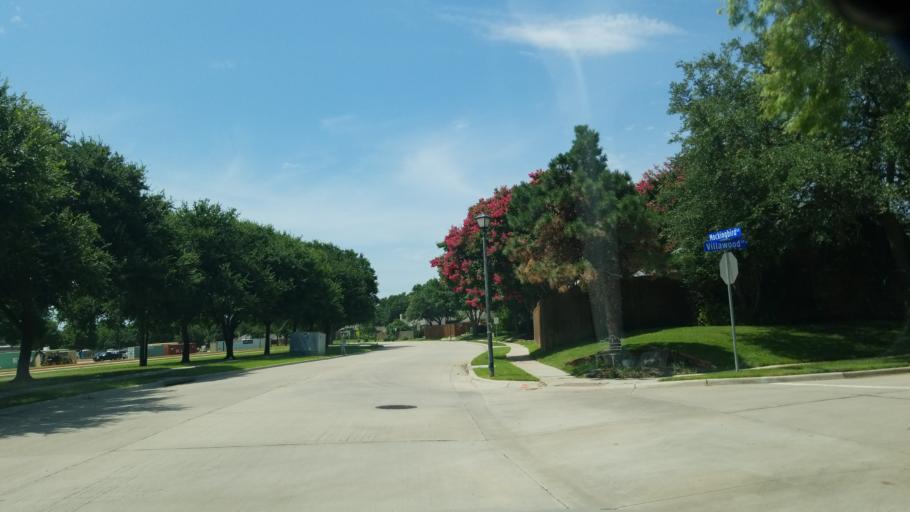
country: US
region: Texas
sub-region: Dallas County
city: Coppell
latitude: 32.9634
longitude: -96.9703
